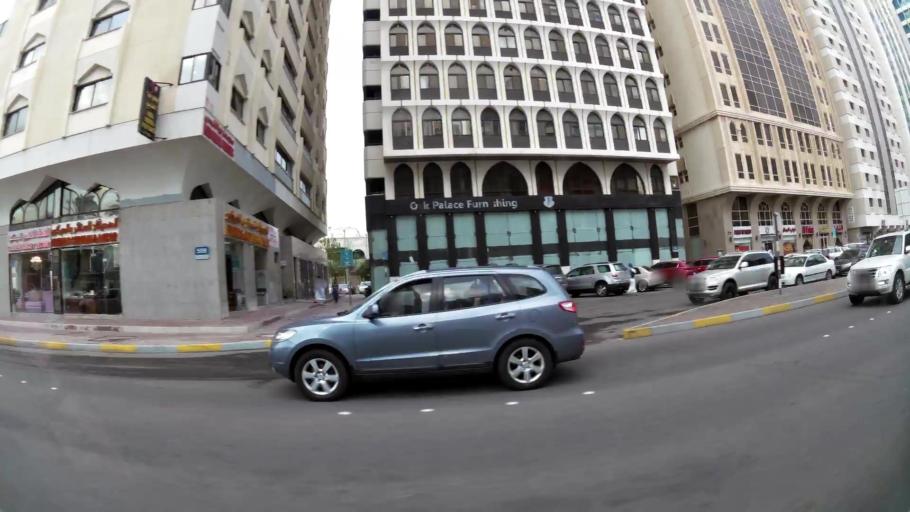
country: AE
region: Abu Dhabi
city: Abu Dhabi
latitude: 24.4741
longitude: 54.3671
